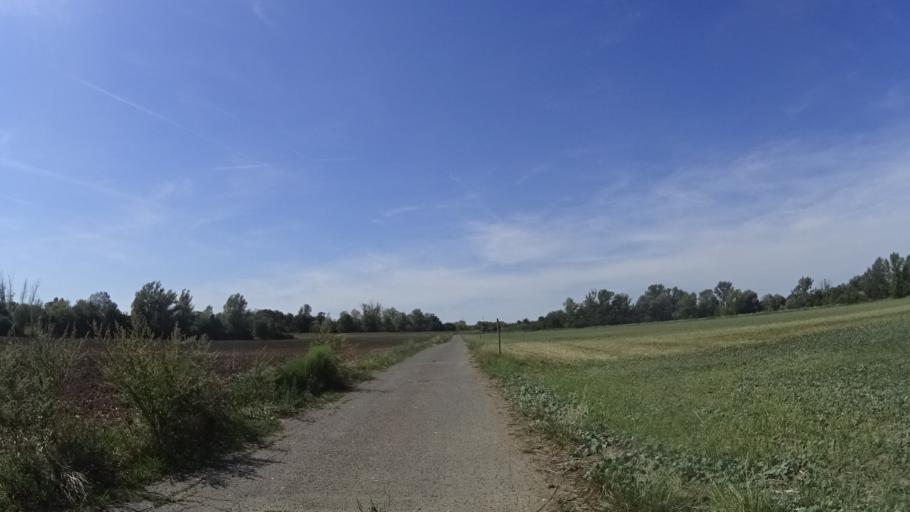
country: AT
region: Lower Austria
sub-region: Politischer Bezirk Ganserndorf
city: Angern an der March
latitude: 48.3740
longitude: 16.8486
